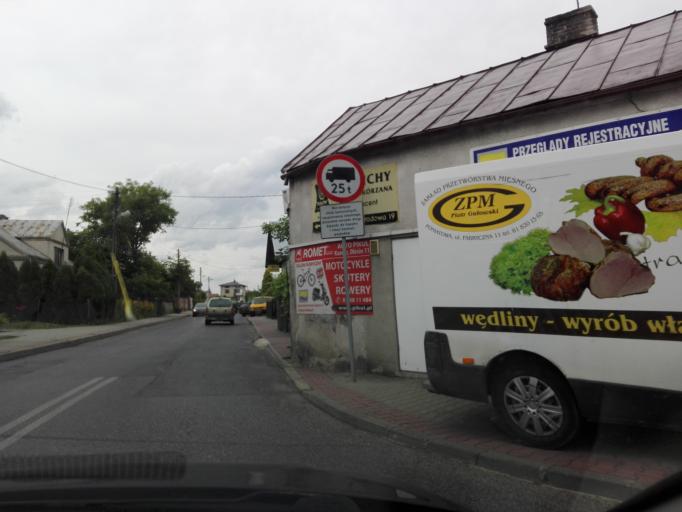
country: PL
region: Lublin Voivodeship
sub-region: Powiat pulawski
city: Kurow
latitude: 51.3891
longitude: 22.1874
